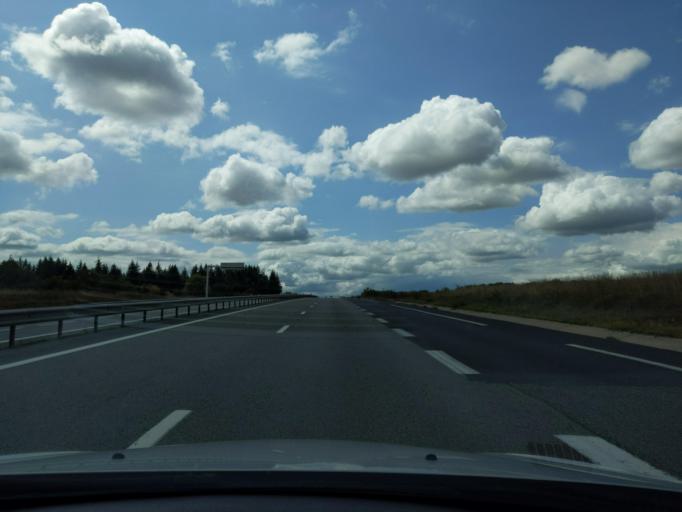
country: FR
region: Limousin
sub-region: Departement de la Creuse
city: Gouzon
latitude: 46.1963
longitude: 2.1842
